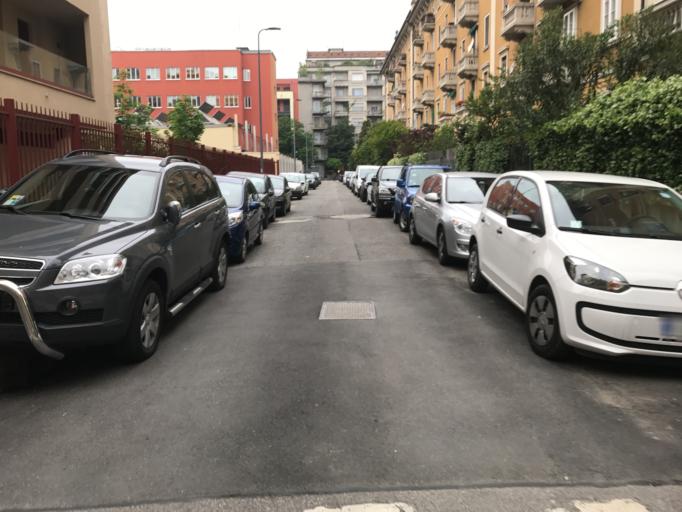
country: IT
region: Lombardy
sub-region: Citta metropolitana di Milano
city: Milano
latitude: 45.4823
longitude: 9.2280
